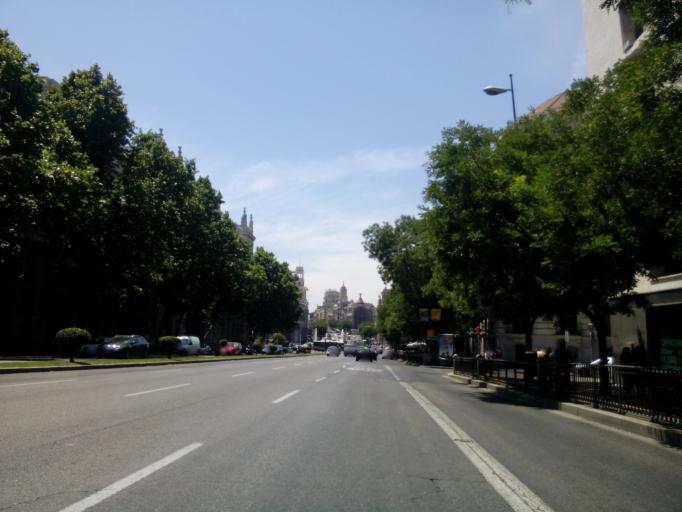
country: ES
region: Madrid
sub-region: Provincia de Madrid
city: Retiro
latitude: 40.4197
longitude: -3.6899
